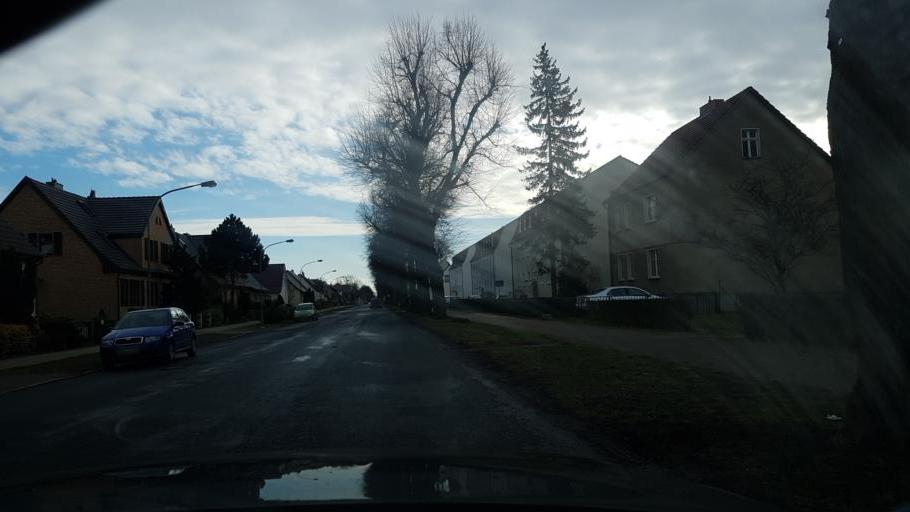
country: DE
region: Brandenburg
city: Kyritz
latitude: 52.9508
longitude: 12.3821
